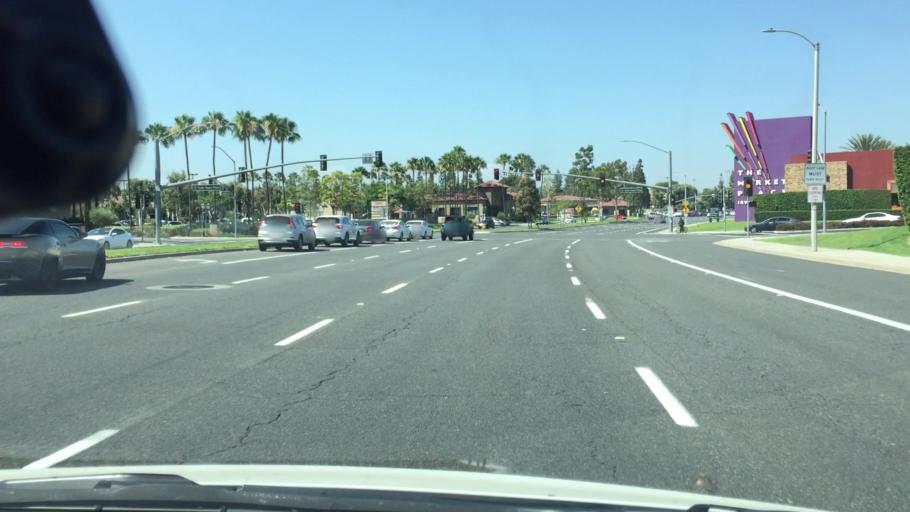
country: US
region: California
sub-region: Orange County
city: North Tustin
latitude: 33.7277
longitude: -117.7888
